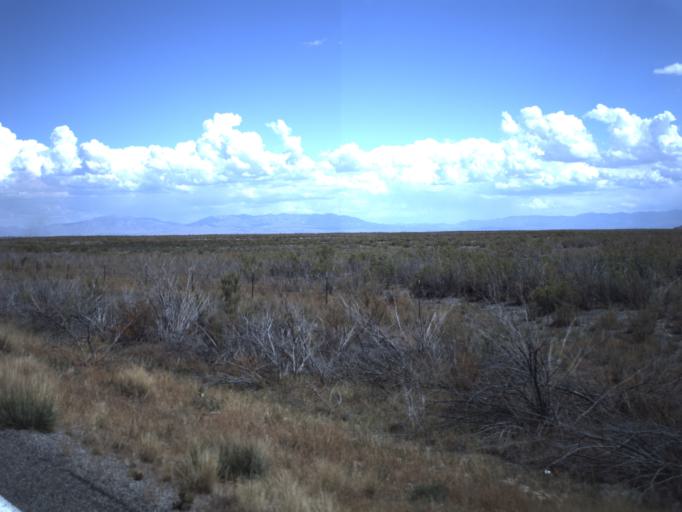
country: US
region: Utah
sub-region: Millard County
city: Delta
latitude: 39.2753
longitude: -112.8545
